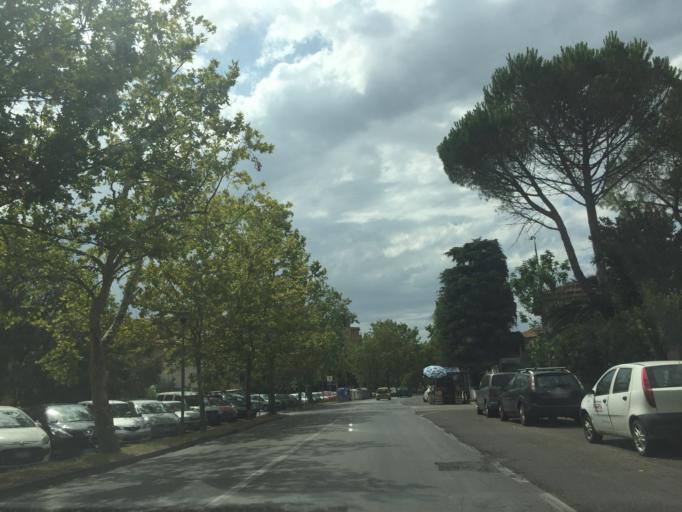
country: IT
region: Tuscany
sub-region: Province of Pisa
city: Pisa
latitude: 43.7251
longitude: 10.4067
